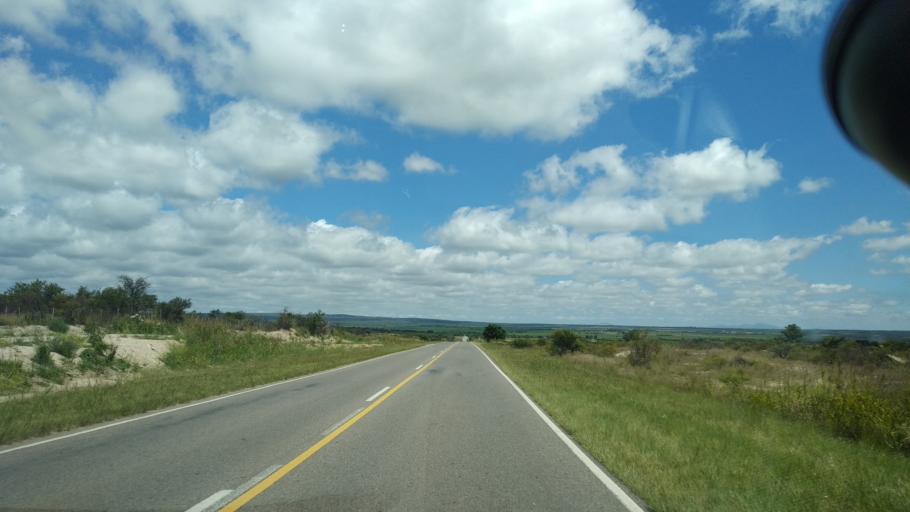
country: AR
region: Cordoba
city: Villa Cura Brochero
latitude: -31.6862
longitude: -65.0768
